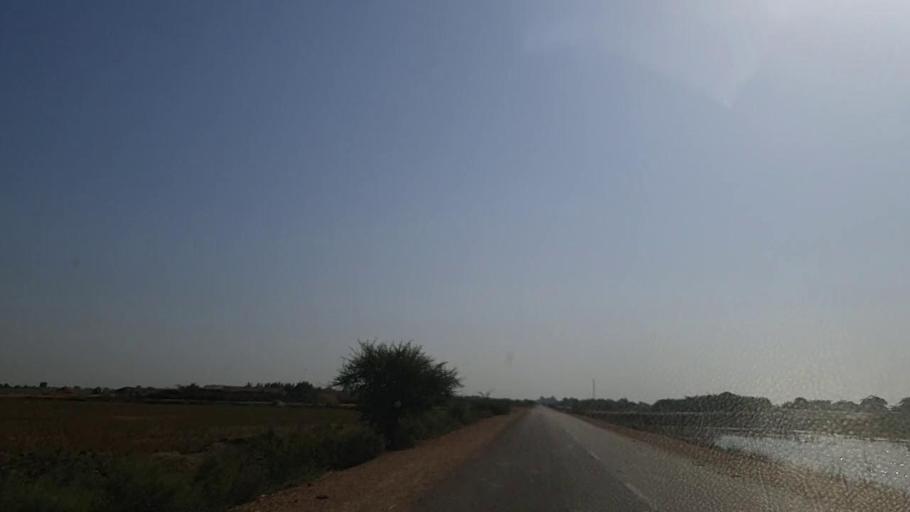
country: PK
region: Sindh
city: Jati
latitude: 24.5293
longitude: 68.2777
